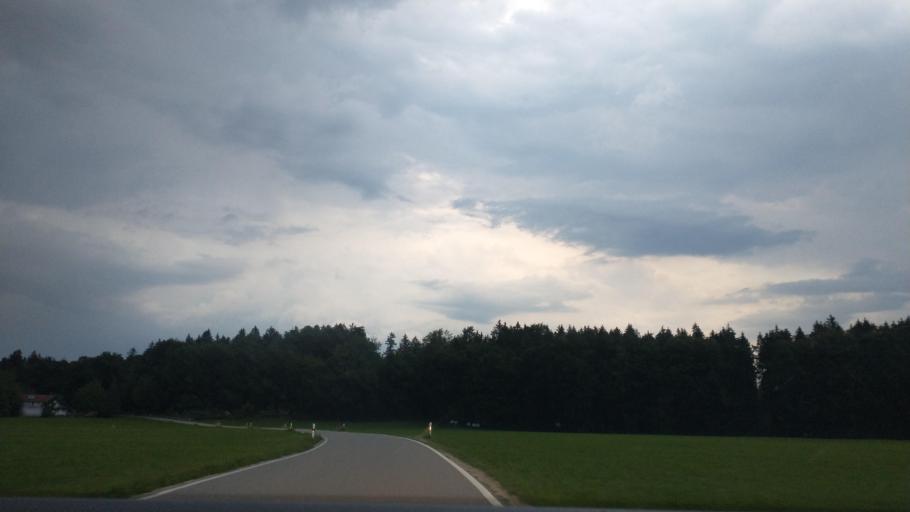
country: DE
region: Baden-Wuerttemberg
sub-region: Tuebingen Region
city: Amtzell
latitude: 47.6889
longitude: 9.7404
